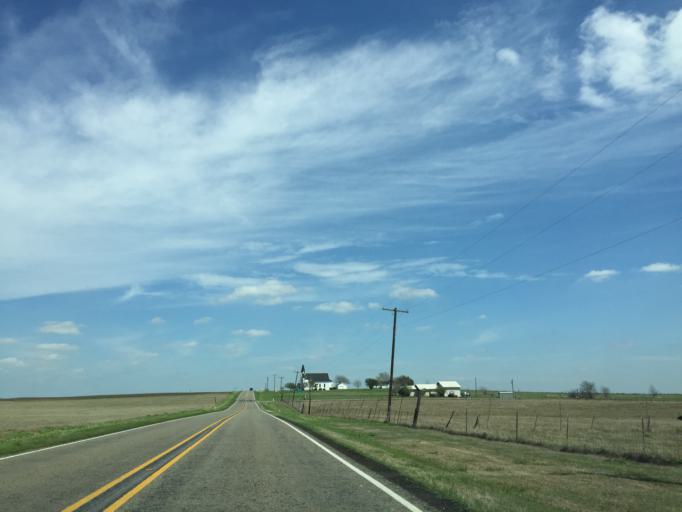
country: US
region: Texas
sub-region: Williamson County
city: Taylor
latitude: 30.5544
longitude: -97.3193
